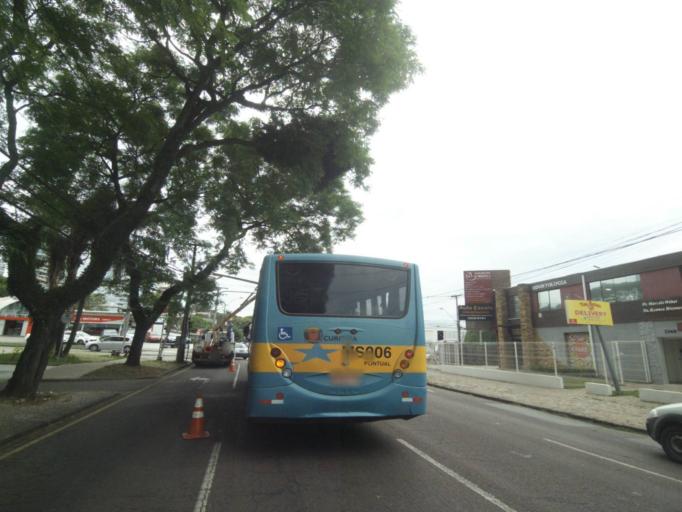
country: BR
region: Parana
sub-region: Curitiba
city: Curitiba
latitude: -25.4346
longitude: -49.3069
